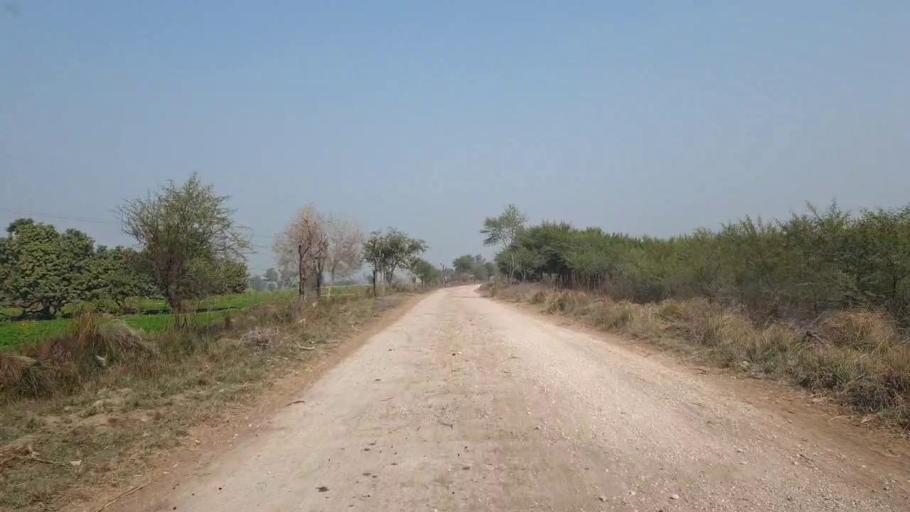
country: PK
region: Sindh
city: Hala
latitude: 25.9721
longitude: 68.4271
